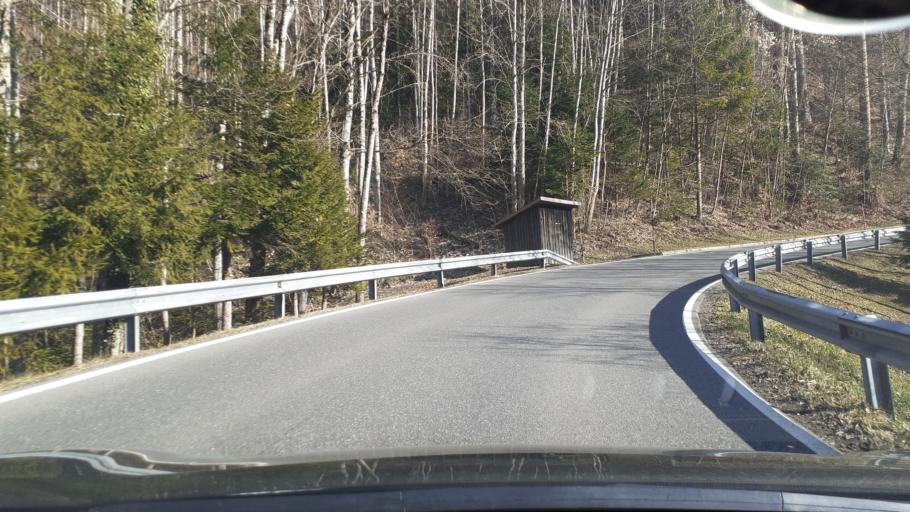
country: AT
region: Vorarlberg
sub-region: Politischer Bezirk Feldkirch
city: Fraxern
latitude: 47.3110
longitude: 9.6665
